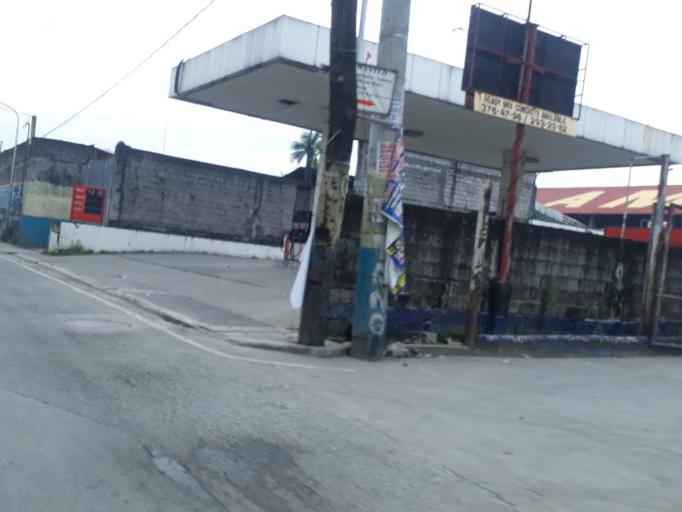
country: PH
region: Metro Manila
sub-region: Caloocan City
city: Niugan
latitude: 14.6820
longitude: 120.9601
